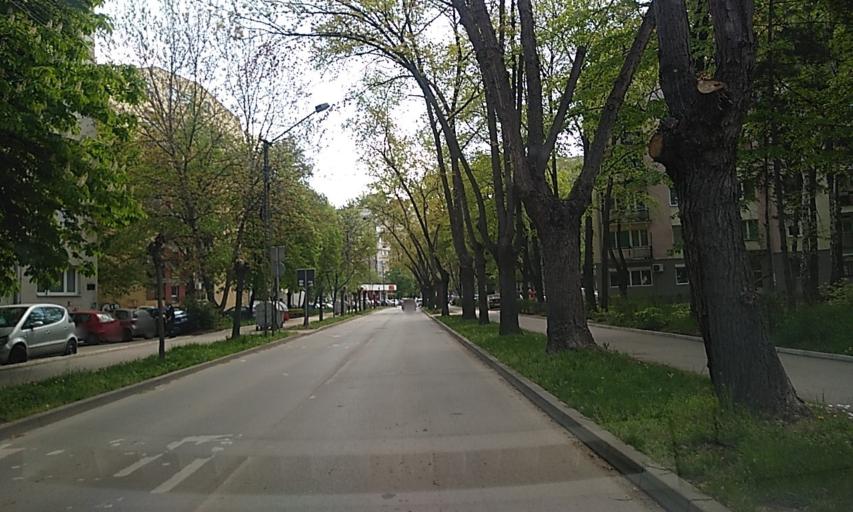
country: RS
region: Central Serbia
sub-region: Nisavski Okrug
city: Nis
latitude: 43.3188
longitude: 21.9168
